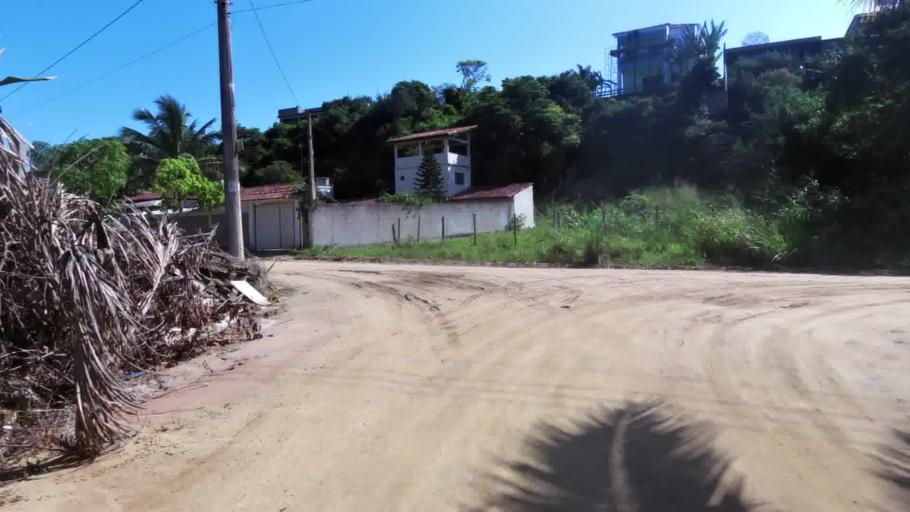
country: BR
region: Espirito Santo
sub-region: Piuma
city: Piuma
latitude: -20.8267
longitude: -40.6199
